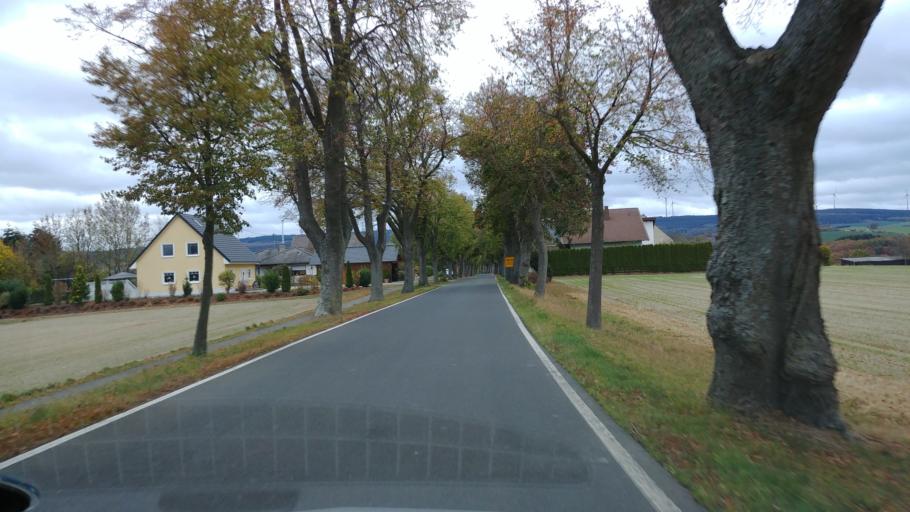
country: DE
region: Rheinland-Pfalz
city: Rorodt
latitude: 49.7942
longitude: 7.0501
